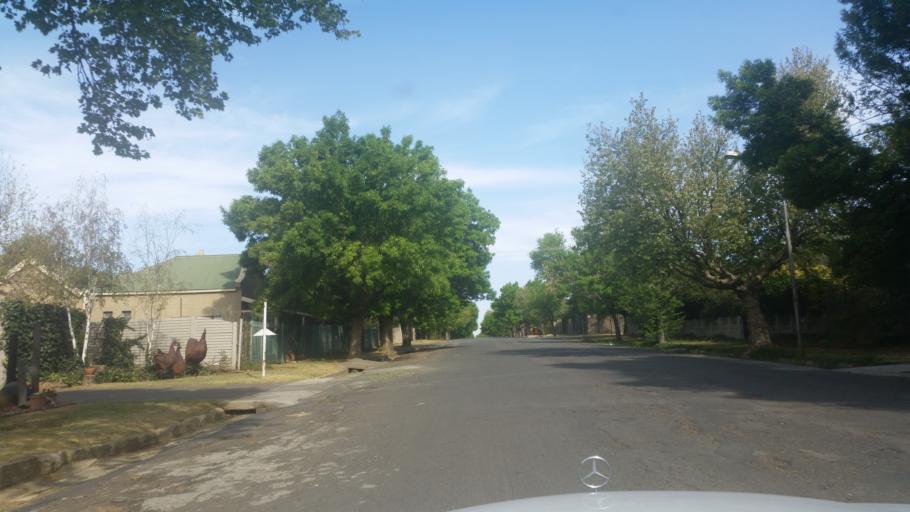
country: ZA
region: Orange Free State
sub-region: Thabo Mofutsanyana District Municipality
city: Harrismith
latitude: -28.2652
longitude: 29.1225
